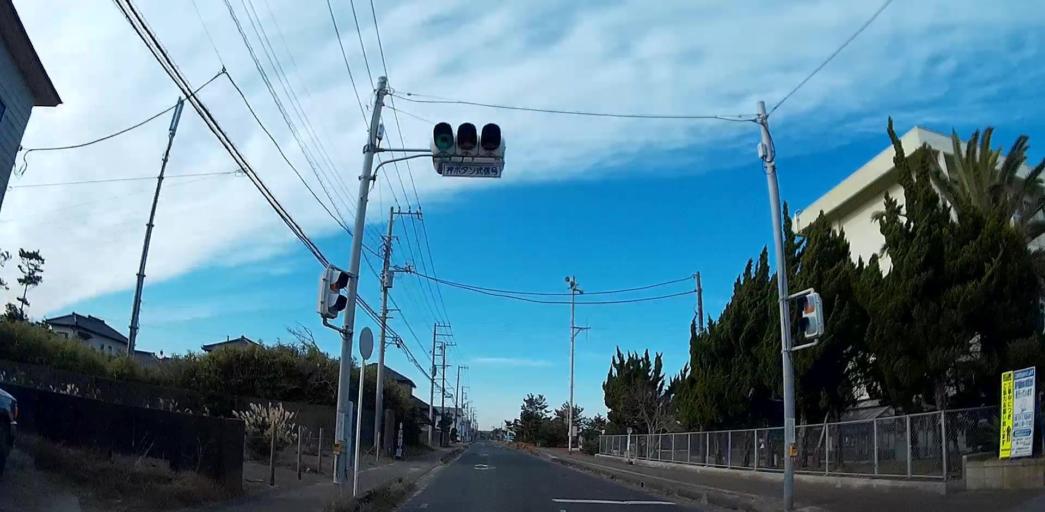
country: JP
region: Chiba
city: Hasaki
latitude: 35.7473
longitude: 140.8344
